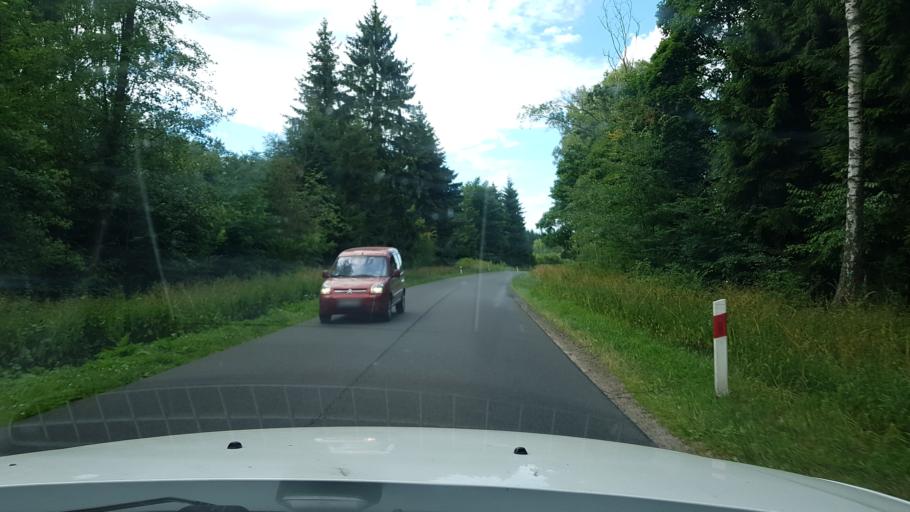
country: PL
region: West Pomeranian Voivodeship
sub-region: Powiat drawski
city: Zlocieniec
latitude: 53.4988
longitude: 16.0294
